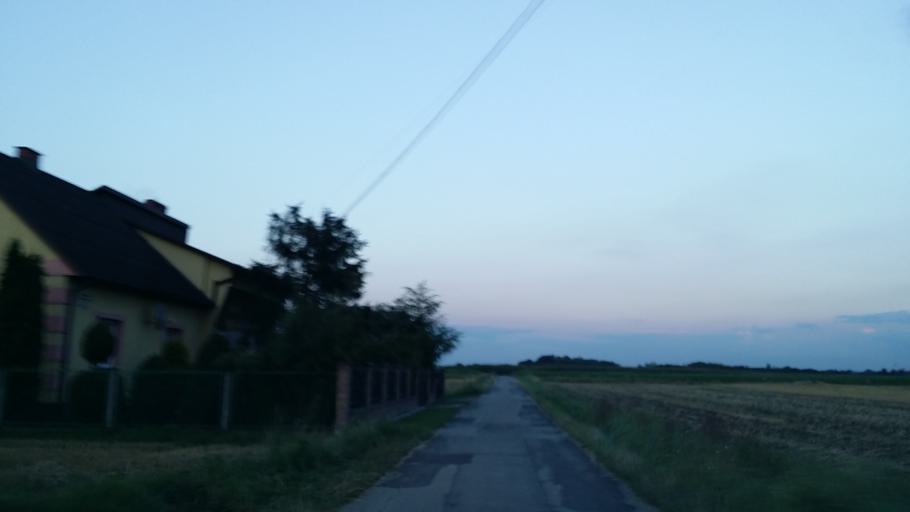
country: PL
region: Lesser Poland Voivodeship
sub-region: Powiat oswiecimski
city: Przeciszow
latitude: 50.0162
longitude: 19.3785
